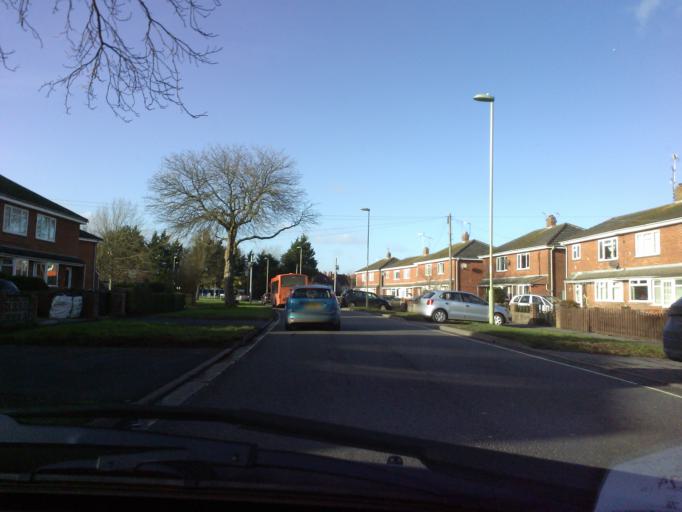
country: GB
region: England
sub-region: Hampshire
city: Romsey
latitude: 50.9931
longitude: -1.4956
